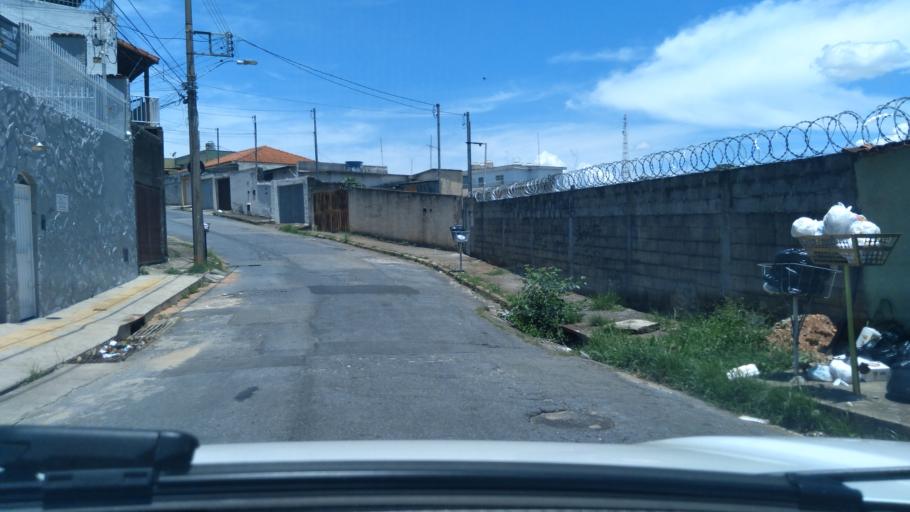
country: BR
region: Minas Gerais
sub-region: Contagem
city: Contagem
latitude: -19.9339
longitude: -43.9969
